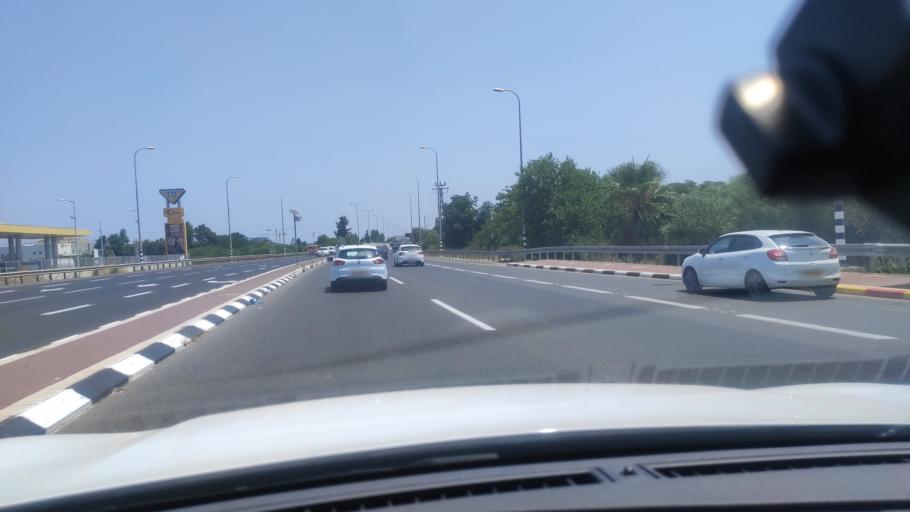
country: IL
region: Central District
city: Kfar Saba
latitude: 32.1518
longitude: 34.9214
